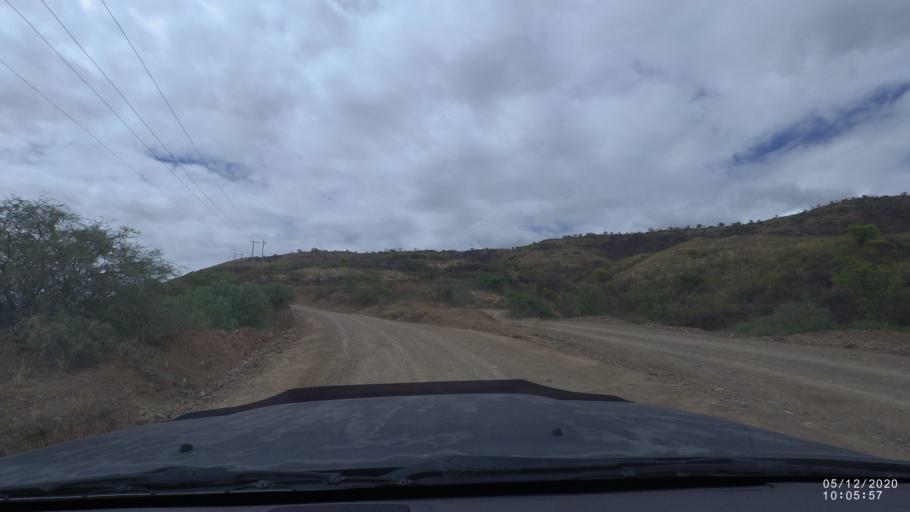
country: BO
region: Cochabamba
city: Sipe Sipe
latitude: -17.4731
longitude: -66.2848
